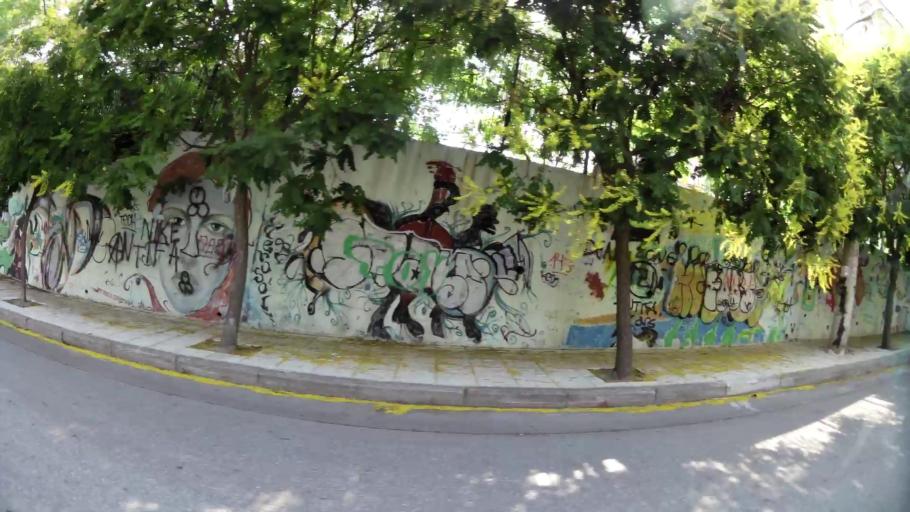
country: GR
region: Central Macedonia
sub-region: Nomos Thessalonikis
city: Sykies
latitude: 40.6568
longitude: 22.9418
